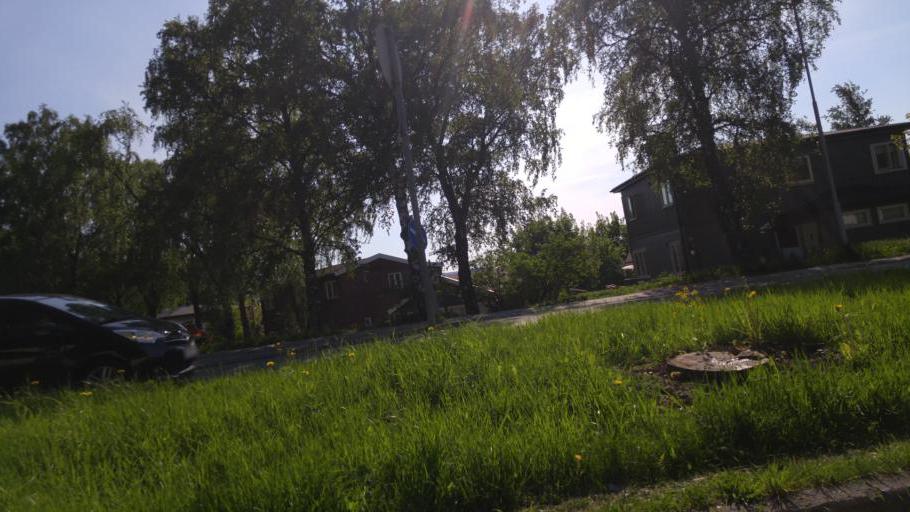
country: NO
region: Sor-Trondelag
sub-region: Trondheim
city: Trondheim
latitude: 63.4179
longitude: 10.4148
